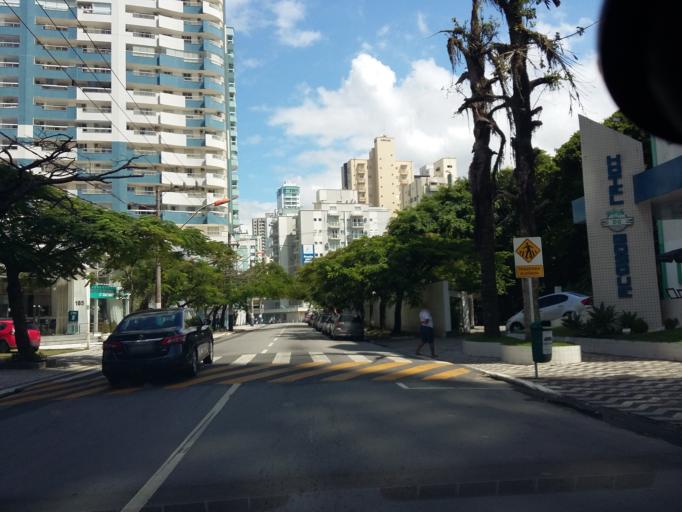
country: BR
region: Santa Catarina
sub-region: Balneario Camboriu
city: Balneario Camboriu
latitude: -26.9749
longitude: -48.6368
